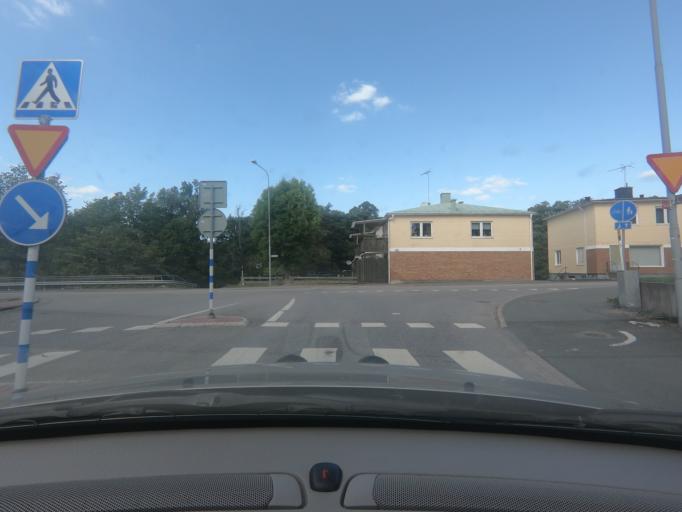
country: SE
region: Joenkoeping
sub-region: Vetlanda Kommun
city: Landsbro
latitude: 57.3691
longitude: 14.9032
